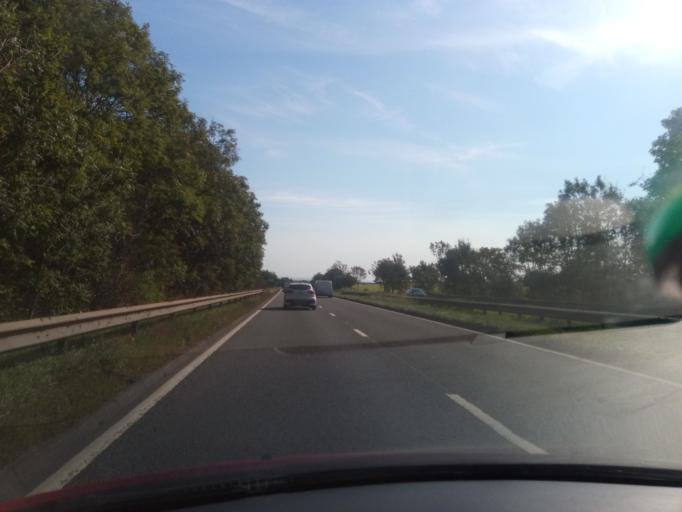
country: GB
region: England
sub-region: Sunderland
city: Ryhope
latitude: 54.8495
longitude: -1.3886
